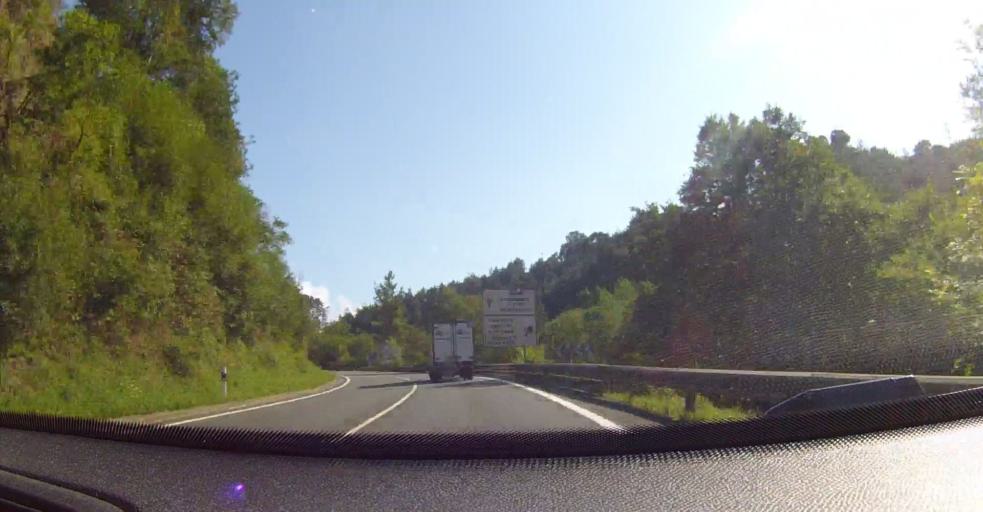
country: ES
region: Basque Country
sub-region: Bizkaia
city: Muxika
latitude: 43.2575
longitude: -2.6914
